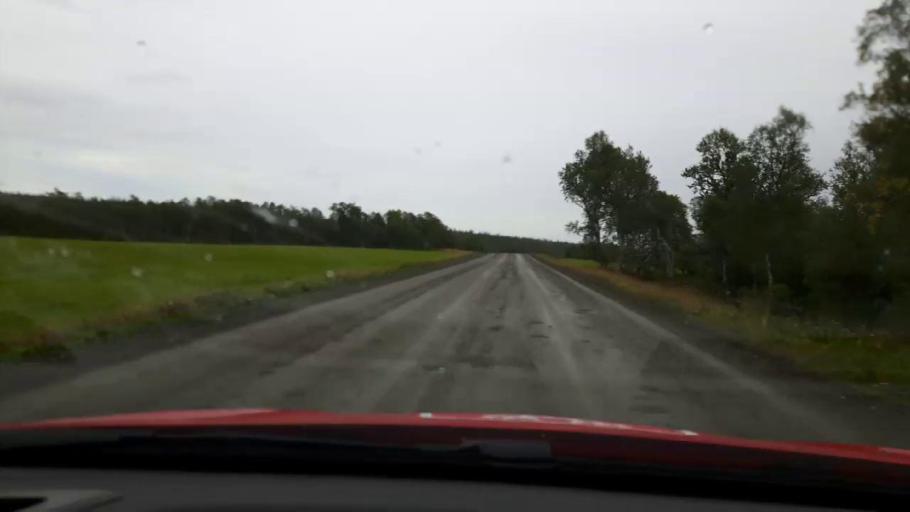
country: NO
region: Nord-Trondelag
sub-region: Meraker
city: Meraker
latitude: 63.5795
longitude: 12.2708
